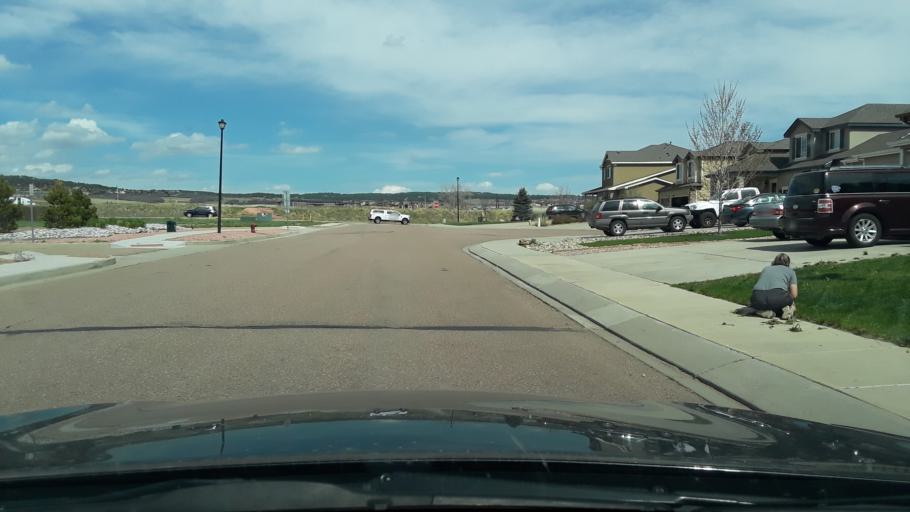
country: US
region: Colorado
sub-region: El Paso County
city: Monument
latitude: 39.0723
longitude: -104.8622
